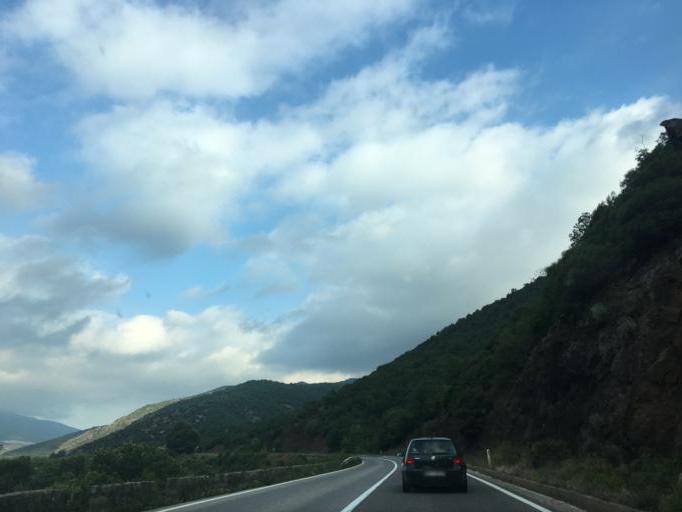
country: MK
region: Demir Kapija
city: Demir Kapija
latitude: 41.3899
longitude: 22.3563
